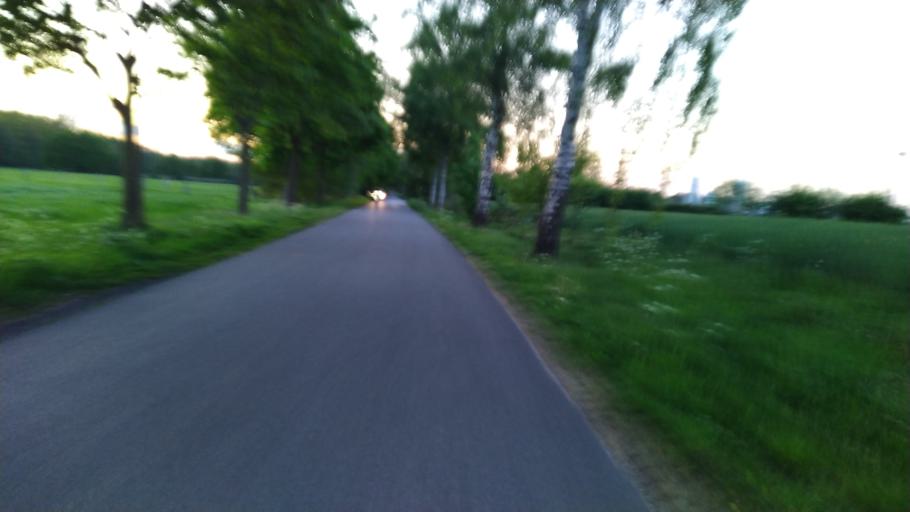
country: DE
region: Lower Saxony
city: Bargstedt
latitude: 53.4749
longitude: 9.4702
